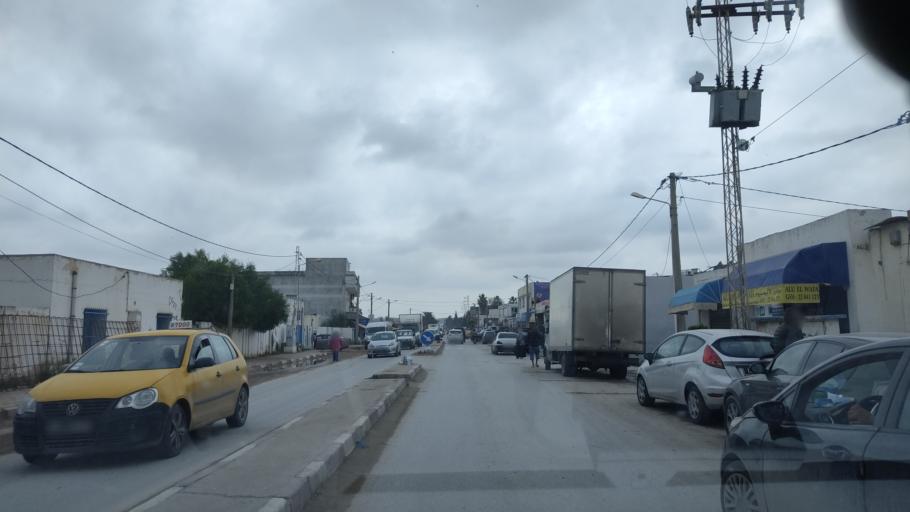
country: TN
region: Ariana
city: Ariana
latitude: 36.8864
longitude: 10.2181
